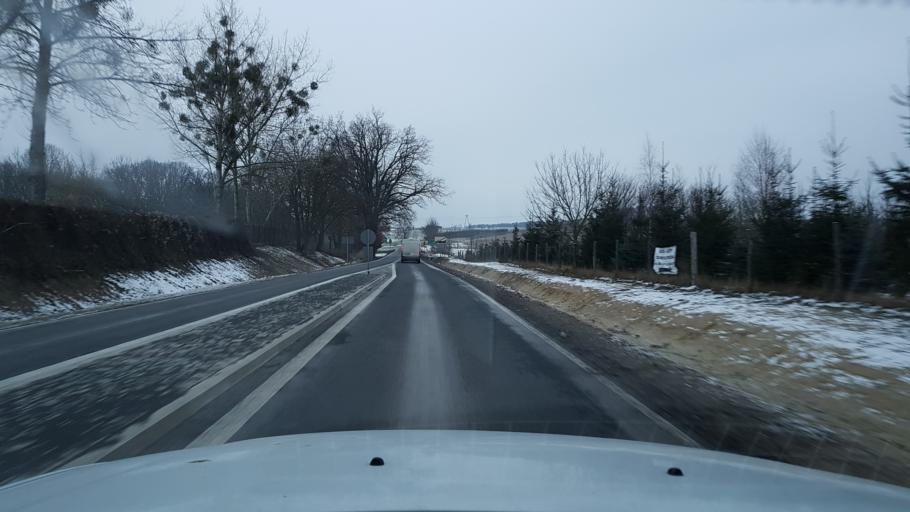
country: PL
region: West Pomeranian Voivodeship
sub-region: Powiat gryfinski
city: Chojna
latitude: 52.9713
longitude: 14.4260
